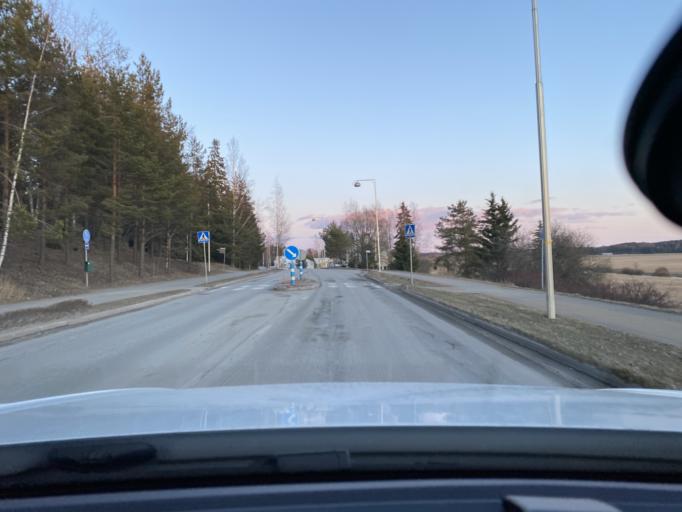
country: FI
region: Pirkanmaa
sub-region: Lounais-Pirkanmaa
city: Punkalaidun
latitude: 61.1104
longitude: 23.1134
